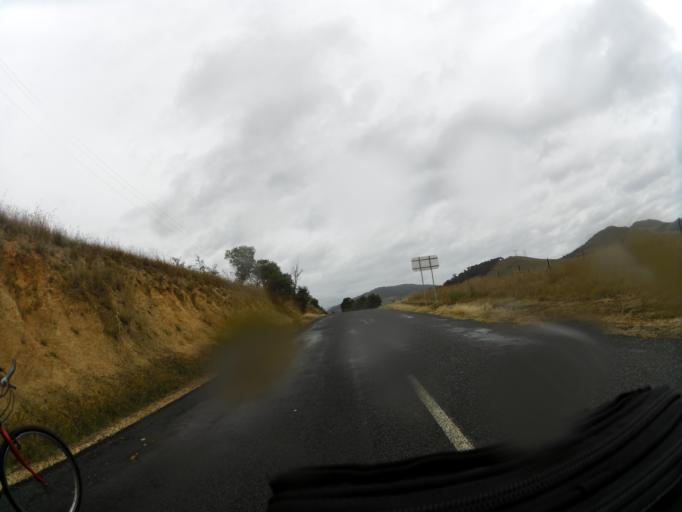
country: AU
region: New South Wales
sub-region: Greater Hume Shire
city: Holbrook
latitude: -36.2241
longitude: 147.6612
